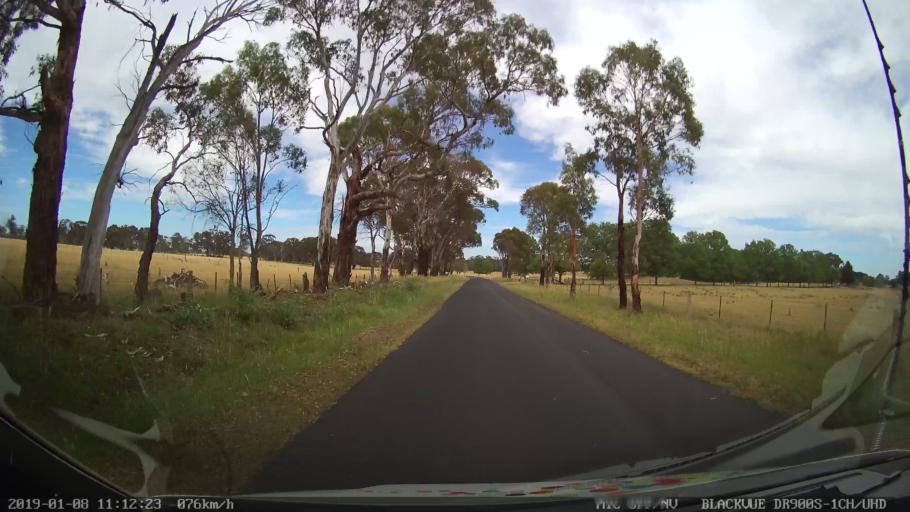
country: AU
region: New South Wales
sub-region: Guyra
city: Guyra
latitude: -30.2280
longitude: 151.6121
